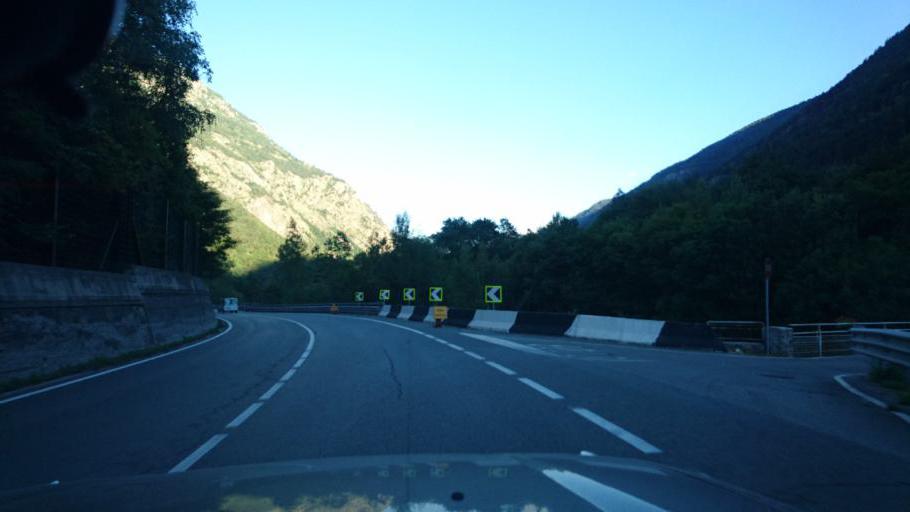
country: IT
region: Aosta Valley
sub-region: Valle d'Aosta
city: La Salle
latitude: 45.7316
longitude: 7.0768
